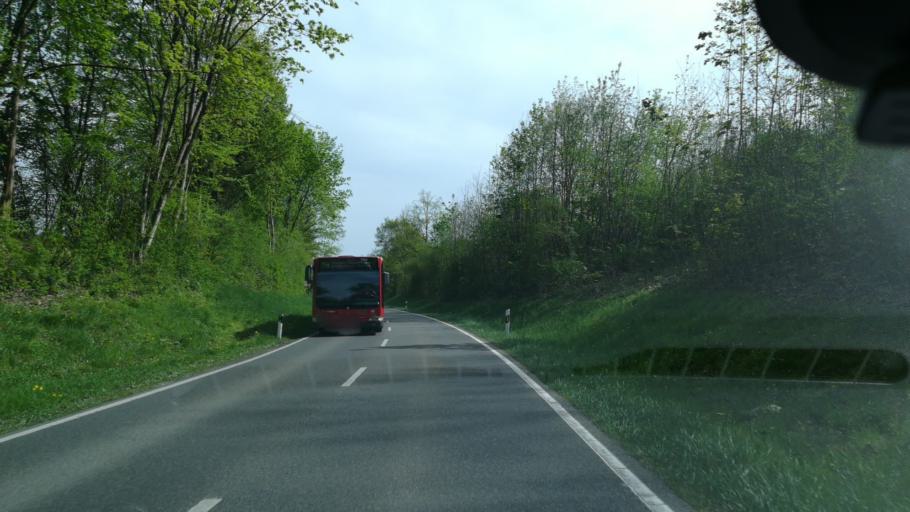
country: DE
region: Baden-Wuerttemberg
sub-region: Freiburg Region
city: Konstanz
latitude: 47.6925
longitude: 9.1890
